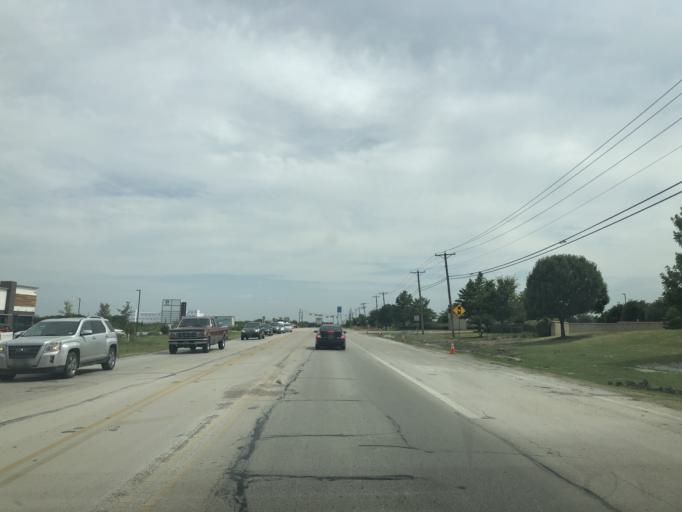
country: US
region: Texas
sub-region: Tarrant County
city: Blue Mound
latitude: 32.8703
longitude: -97.3425
